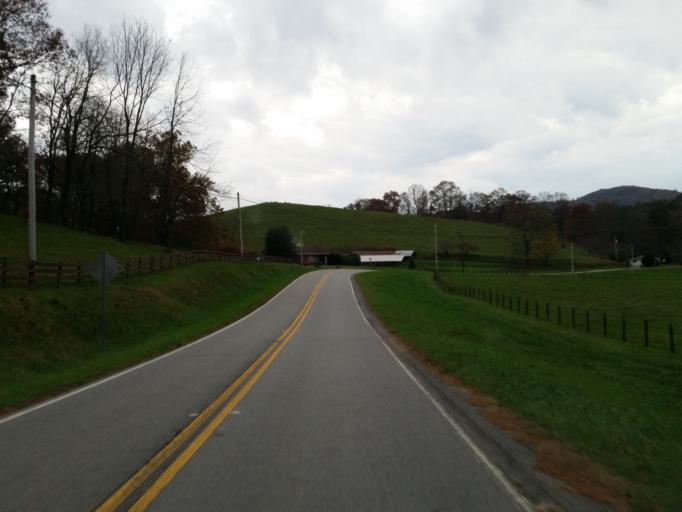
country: US
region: Georgia
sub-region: Lumpkin County
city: Dahlonega
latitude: 34.7112
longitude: -84.0664
